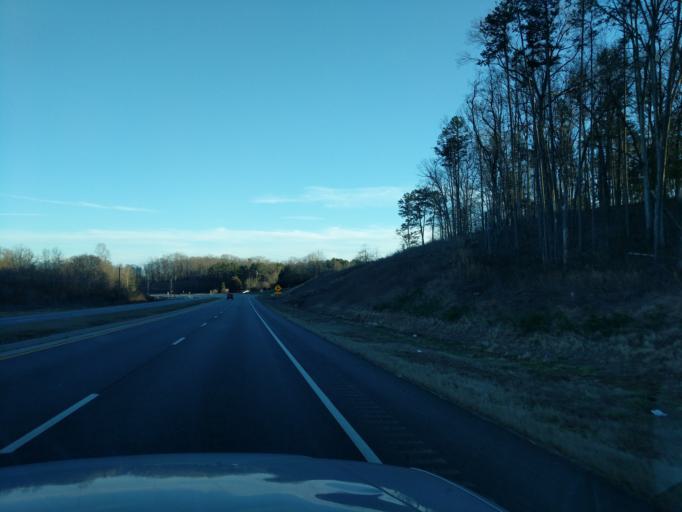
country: US
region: Georgia
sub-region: Stephens County
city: Toccoa
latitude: 34.5383
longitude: -83.2655
